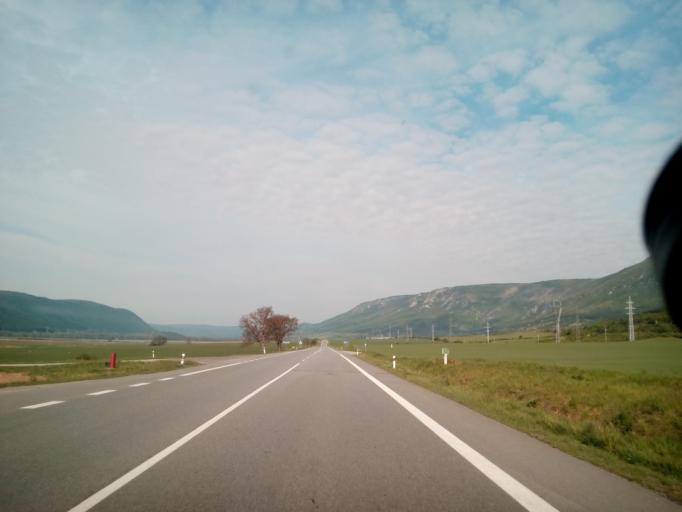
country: SK
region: Kosicky
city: Medzev
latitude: 48.6000
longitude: 20.8038
